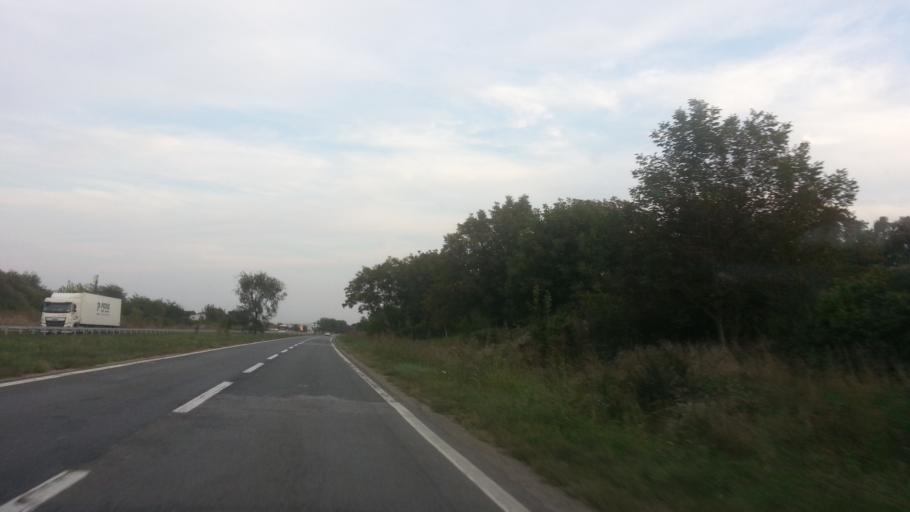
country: RS
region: Central Serbia
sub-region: Belgrade
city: Zemun
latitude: 44.8776
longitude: 20.3250
